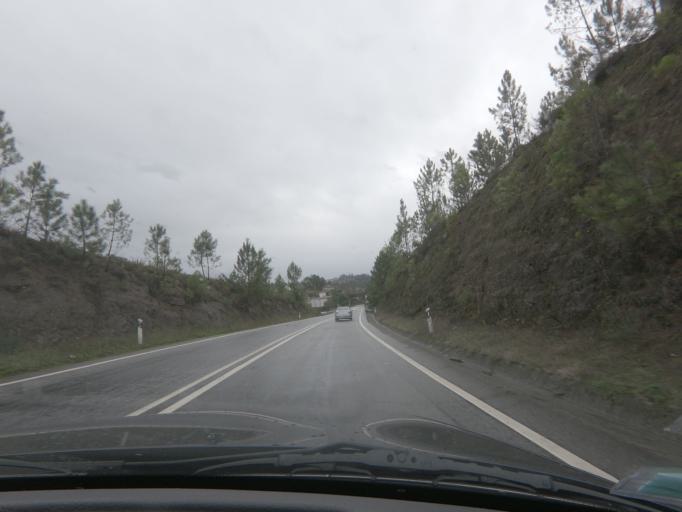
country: PT
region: Porto
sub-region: Amarante
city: Teloes
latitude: 41.3228
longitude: -8.0632
